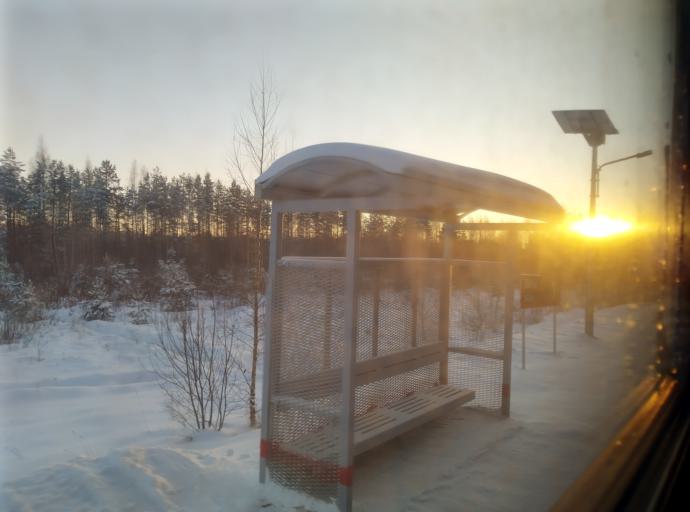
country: RU
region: Tverskaya
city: Ves'yegonsk
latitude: 58.6013
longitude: 37.1336
